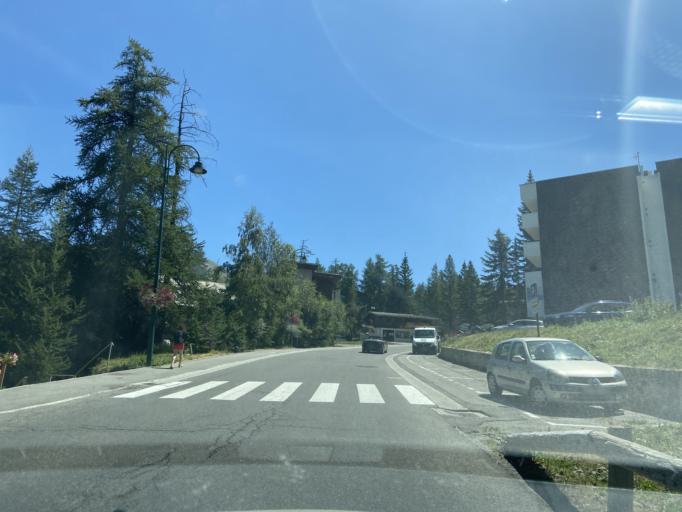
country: FR
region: Provence-Alpes-Cote d'Azur
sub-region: Departement des Hautes-Alpes
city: Guillestre
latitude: 44.5714
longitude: 6.6822
